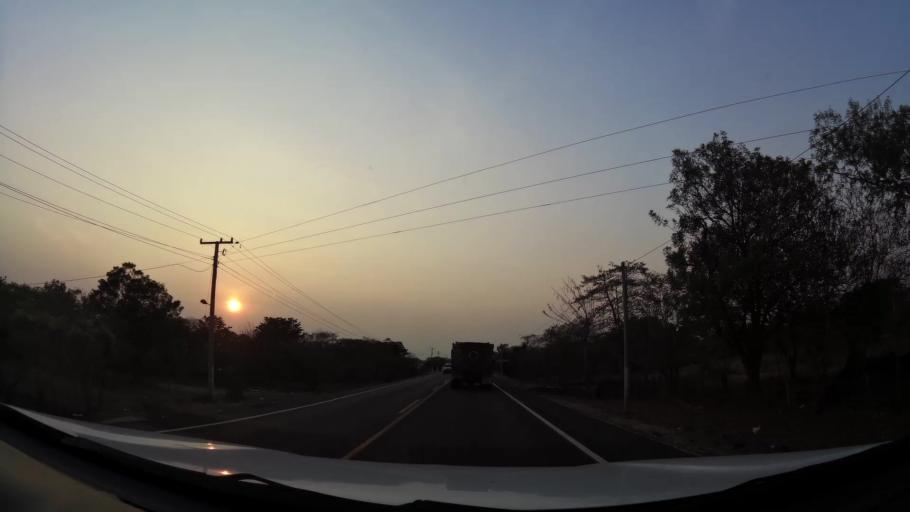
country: NI
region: Leon
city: La Paz Centro
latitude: 12.3119
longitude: -86.7850
